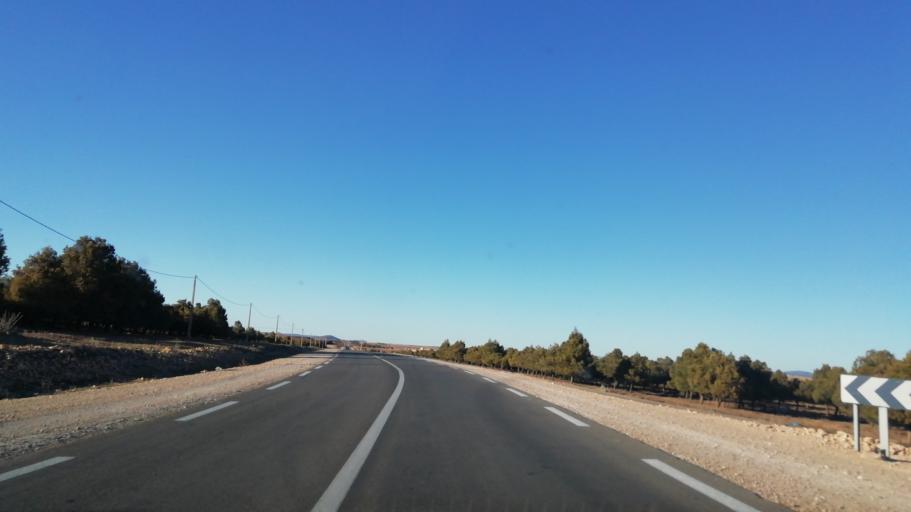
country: DZ
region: Tlemcen
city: Sebdou
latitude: 34.5020
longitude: -1.2777
